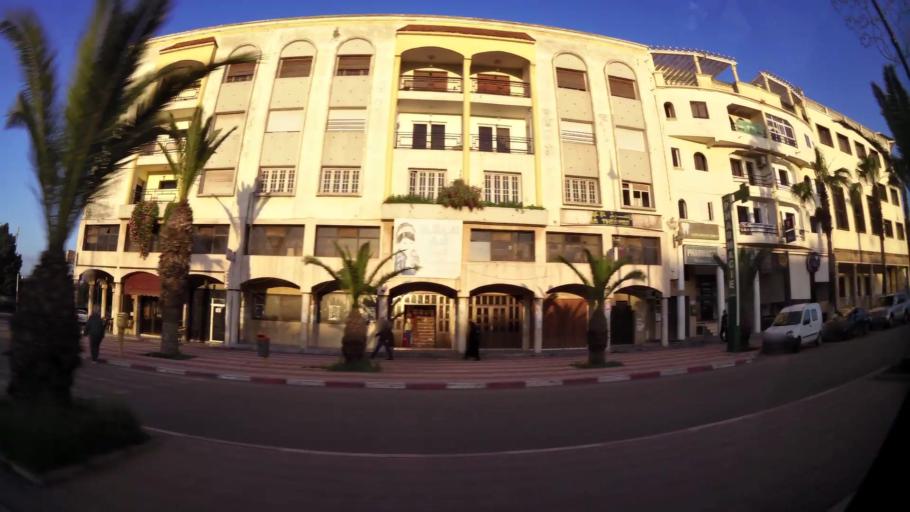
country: MA
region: Chaouia-Ouardigha
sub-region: Settat Province
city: Settat
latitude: 32.9988
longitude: -7.6203
